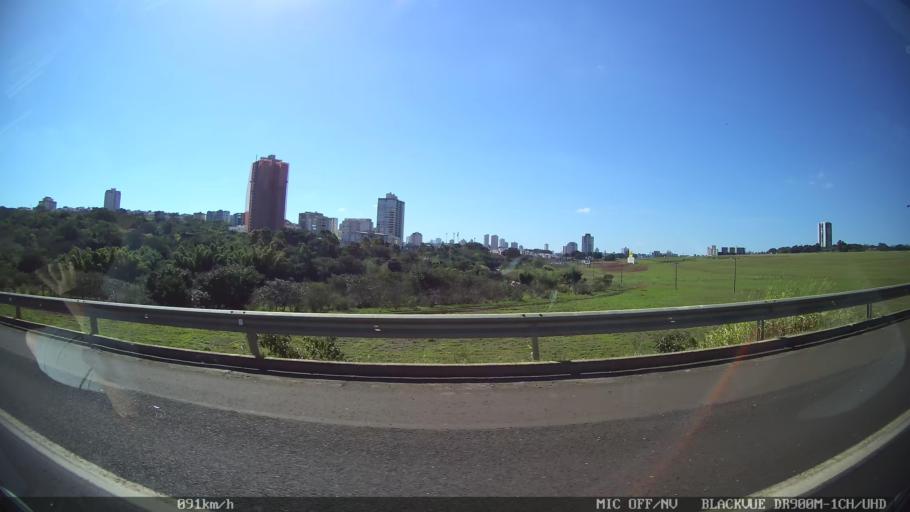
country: BR
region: Sao Paulo
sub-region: Franca
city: Franca
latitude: -20.5583
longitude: -47.4166
